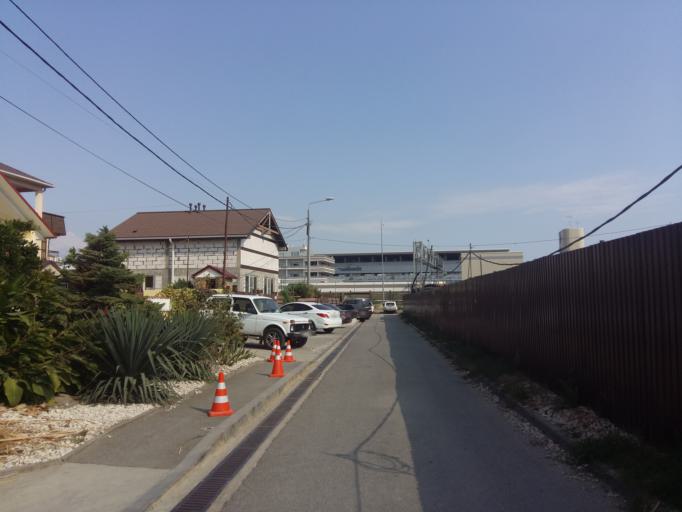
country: RU
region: Krasnodarskiy
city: Adler
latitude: 43.4103
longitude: 39.9642
